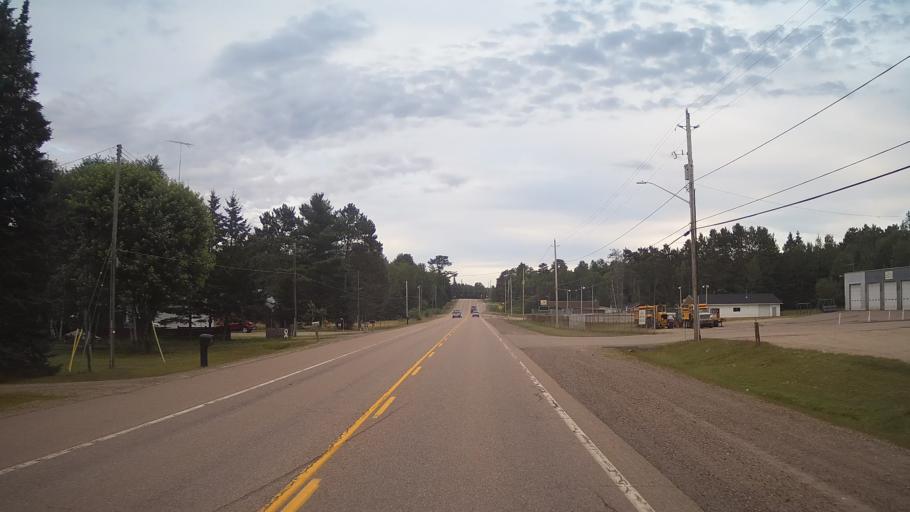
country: CA
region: Ontario
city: Deep River
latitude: 46.1349
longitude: -77.5546
